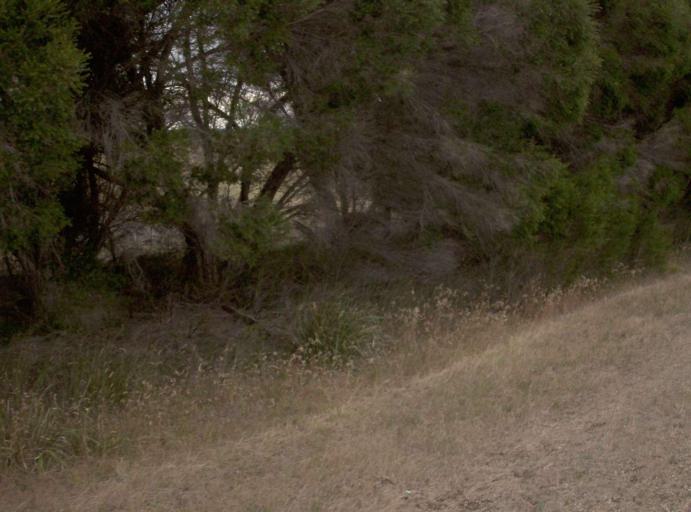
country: AU
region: Victoria
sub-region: East Gippsland
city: Bairnsdale
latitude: -37.9558
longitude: 147.5057
